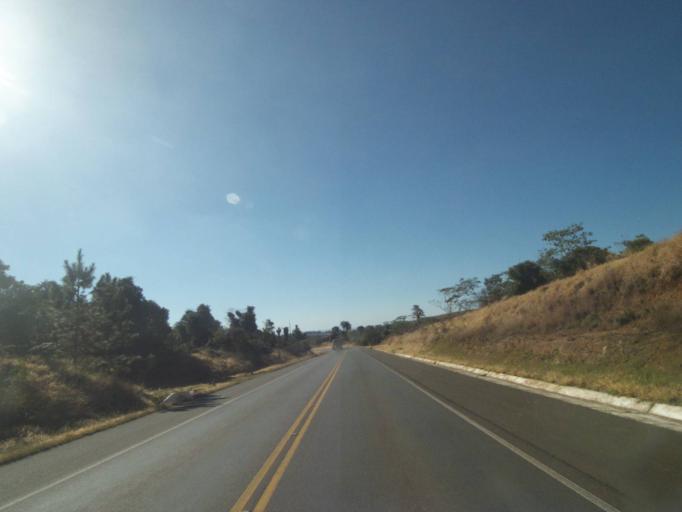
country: BR
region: Parana
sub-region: Tibagi
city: Tibagi
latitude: -24.7246
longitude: -50.4511
